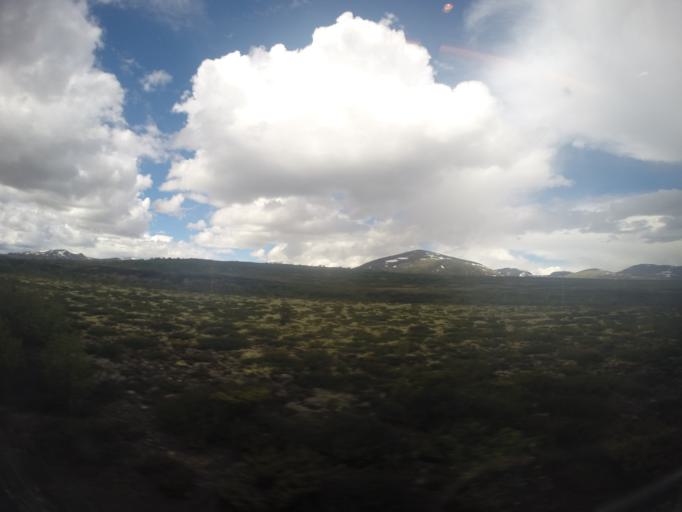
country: NO
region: Sor-Trondelag
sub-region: Oppdal
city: Oppdal
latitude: 62.2477
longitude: 9.5379
